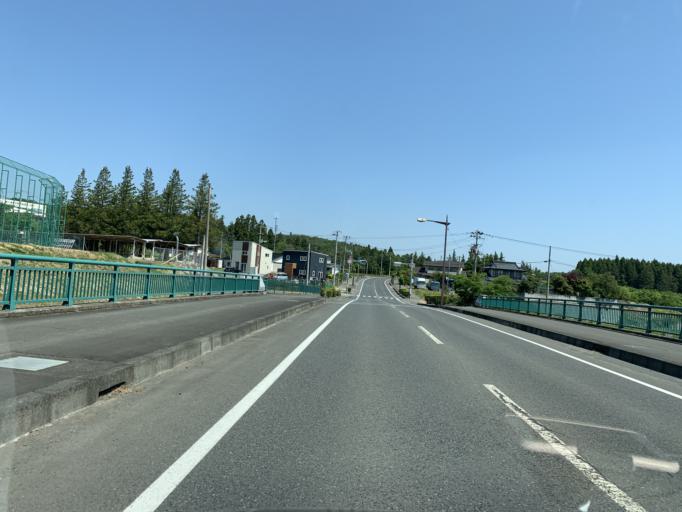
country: JP
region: Iwate
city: Kitakami
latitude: 39.2058
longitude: 141.0948
